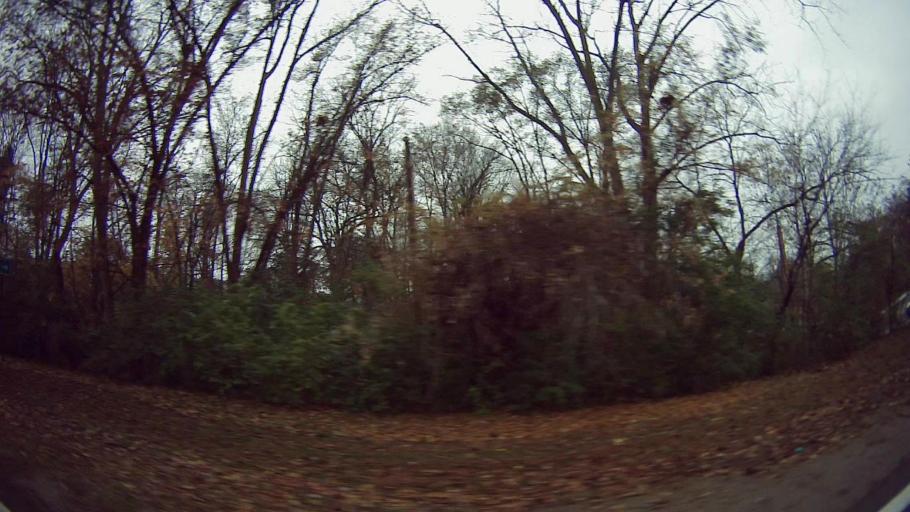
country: US
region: Michigan
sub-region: Oakland County
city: Beverly Hills
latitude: 42.5316
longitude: -83.2449
